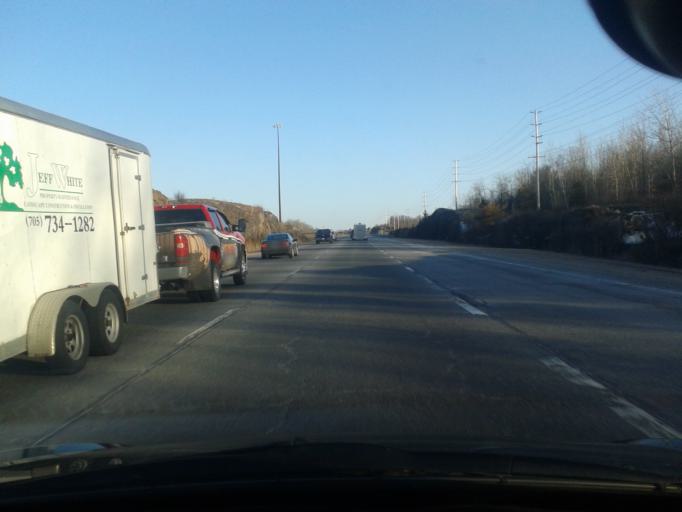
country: CA
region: Ontario
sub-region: Nipissing District
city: North Bay
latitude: 46.3022
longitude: -79.4302
